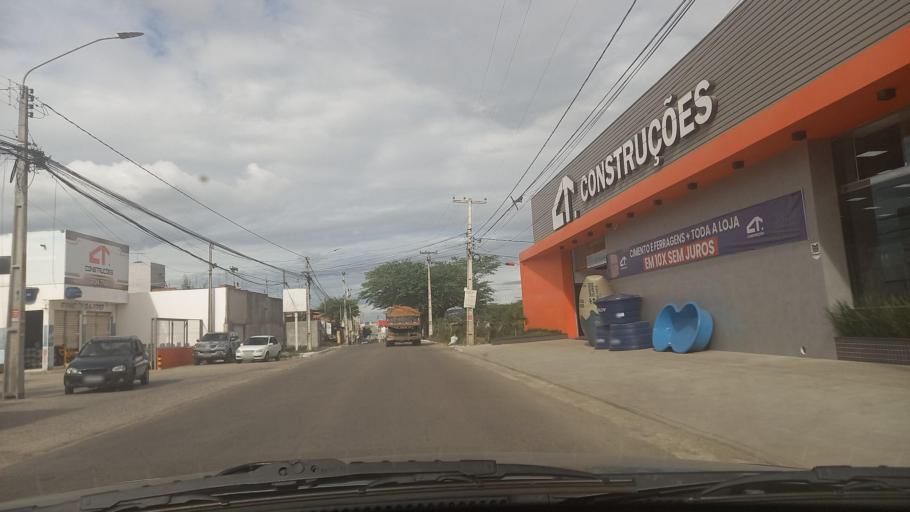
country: BR
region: Pernambuco
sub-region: Caruaru
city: Caruaru
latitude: -8.2857
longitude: -35.9995
